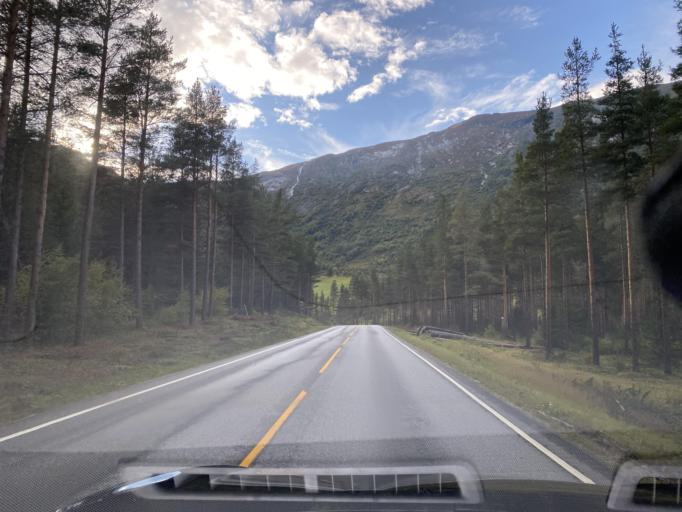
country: NO
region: Oppland
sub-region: Lom
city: Fossbergom
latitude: 61.8089
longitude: 8.4666
